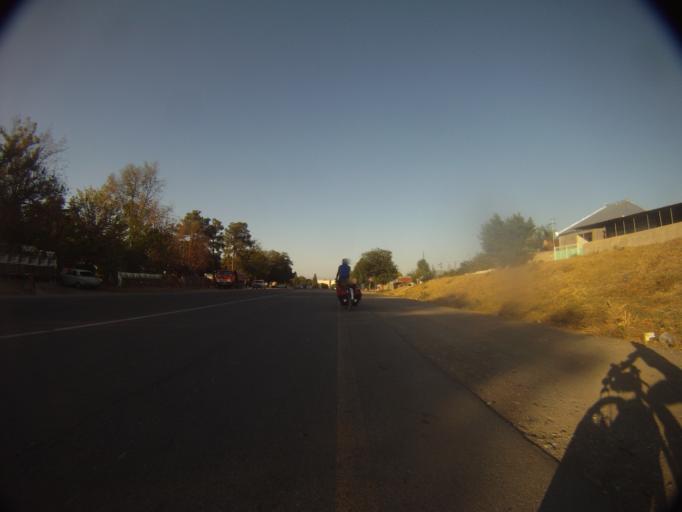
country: AZ
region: Qazax
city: Qazax
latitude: 41.0939
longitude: 45.4003
